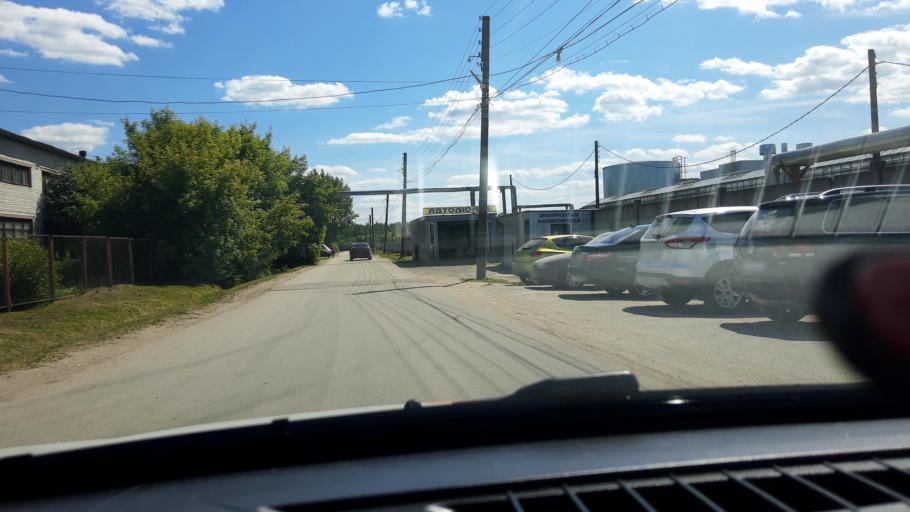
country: RU
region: Nizjnij Novgorod
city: Gorbatovka
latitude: 56.3068
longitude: 43.8142
